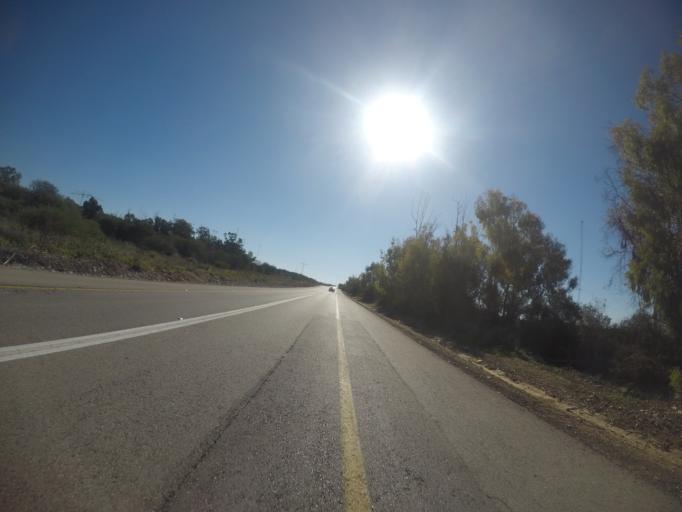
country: IL
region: Southern District
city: Ashqelon
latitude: 31.6984
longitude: 34.6477
